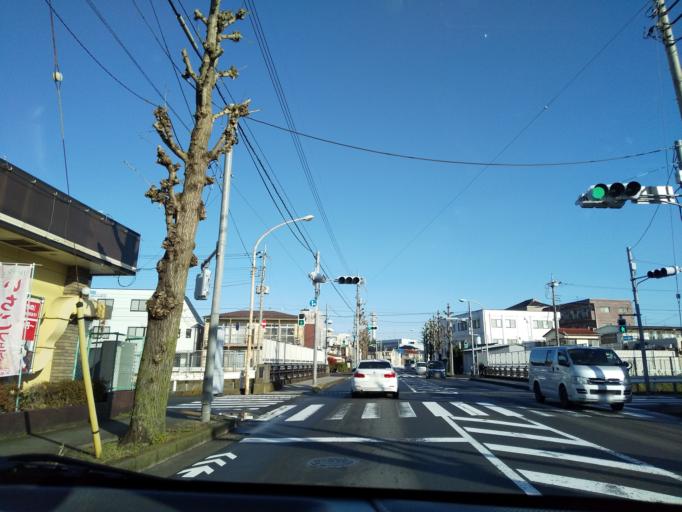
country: JP
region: Tokyo
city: Hachioji
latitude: 35.6609
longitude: 139.3585
